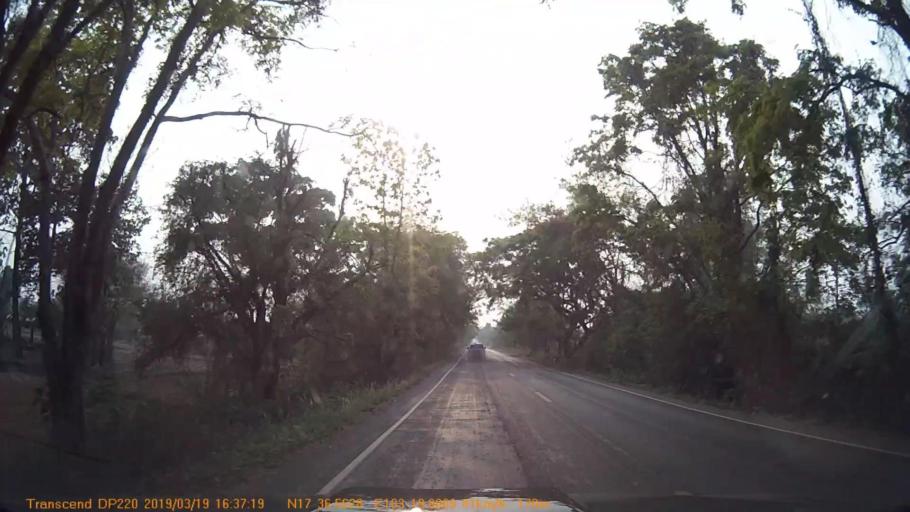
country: TH
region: Changwat Udon Thani
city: Ban Dung
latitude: 17.6094
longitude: 103.3175
